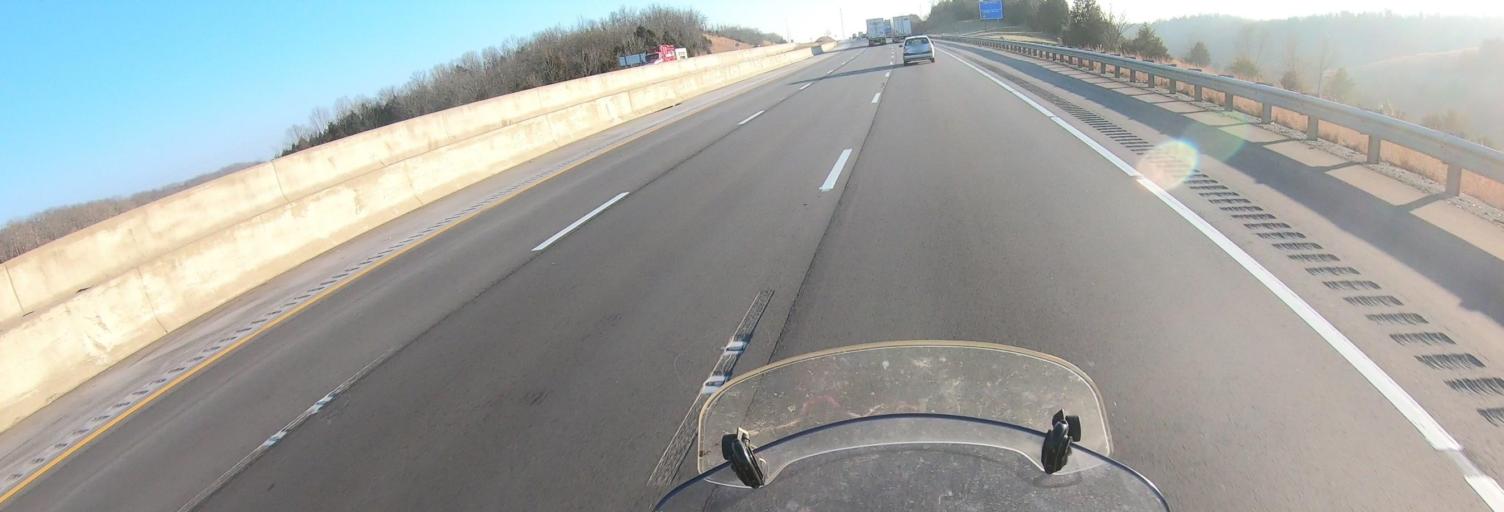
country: US
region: Kentucky
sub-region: Grant County
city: Williamstown
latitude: 38.5046
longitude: -84.5900
